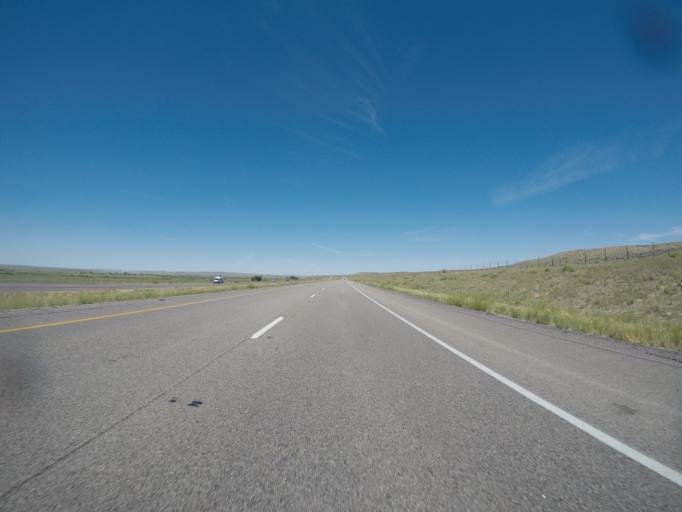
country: US
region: Wyoming
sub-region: Carbon County
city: Saratoga
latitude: 41.7367
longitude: -106.7460
